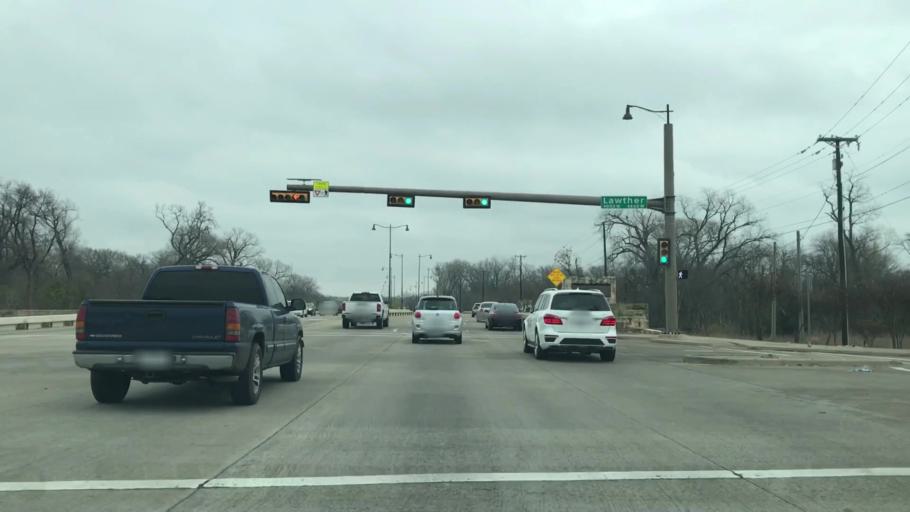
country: US
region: Texas
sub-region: Dallas County
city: Highland Park
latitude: 32.8554
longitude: -96.7316
